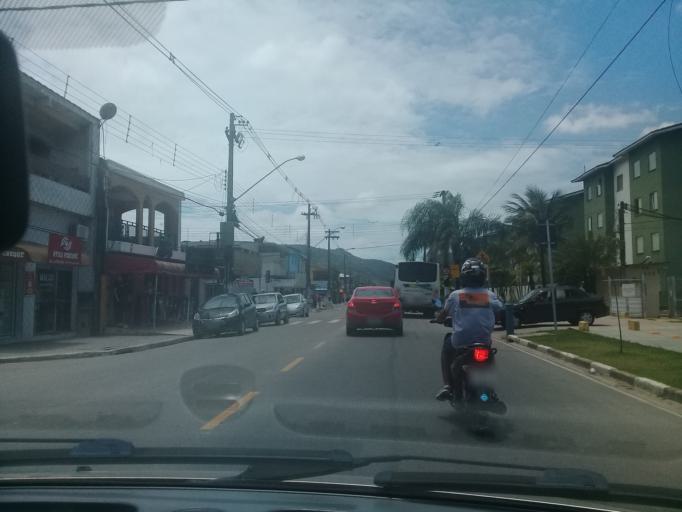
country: BR
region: Sao Paulo
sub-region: Guaruja
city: Guaruja
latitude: -23.9663
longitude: -46.2547
